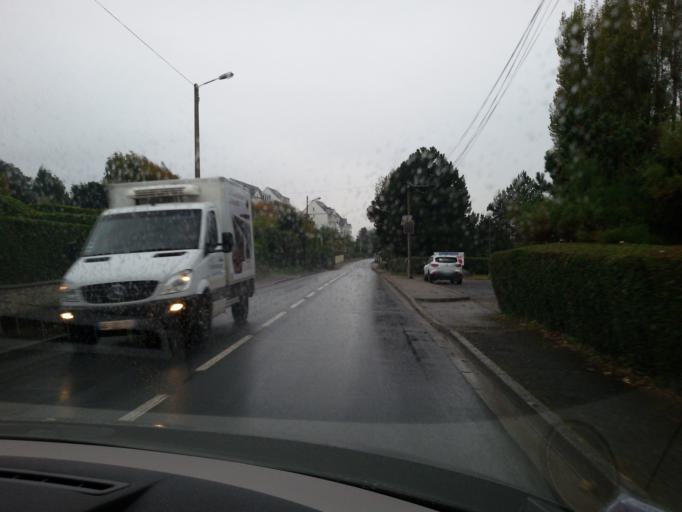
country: FR
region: Lower Normandy
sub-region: Departement du Calvados
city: Trouville-sur-Mer
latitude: 49.3738
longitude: 0.0875
